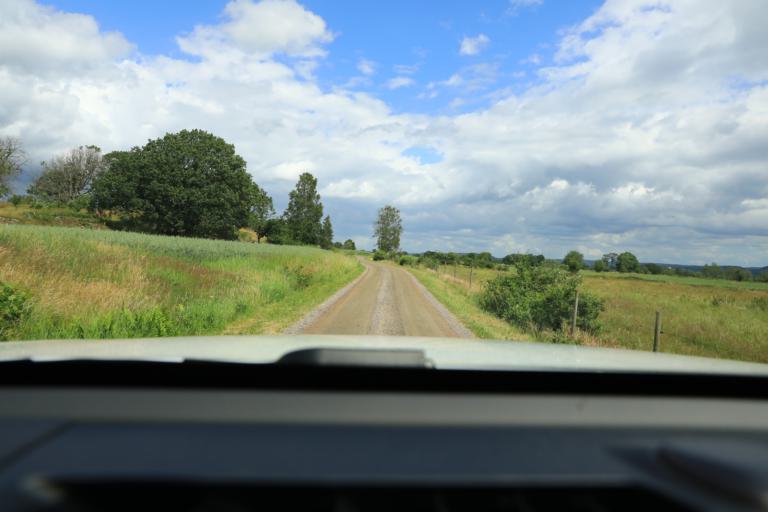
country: SE
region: Halland
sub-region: Varbergs Kommun
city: Tvaaker
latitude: 57.0977
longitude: 12.3973
